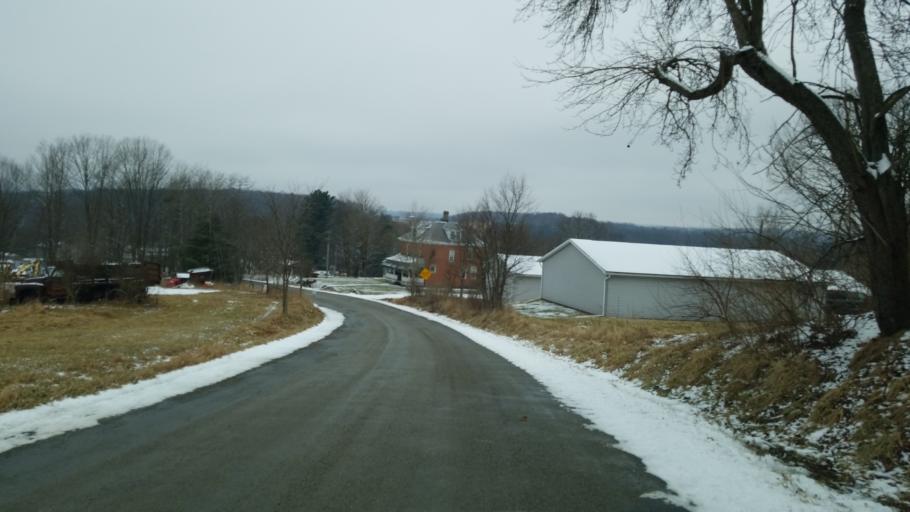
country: US
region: Pennsylvania
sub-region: Jefferson County
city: Reynoldsville
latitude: 41.0880
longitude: -78.8533
